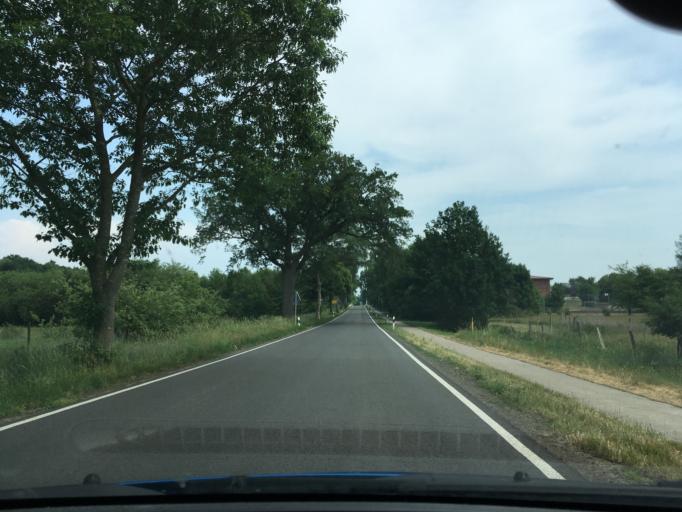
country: DE
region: Lower Saxony
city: Hanstedt
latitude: 53.2594
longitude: 10.0012
